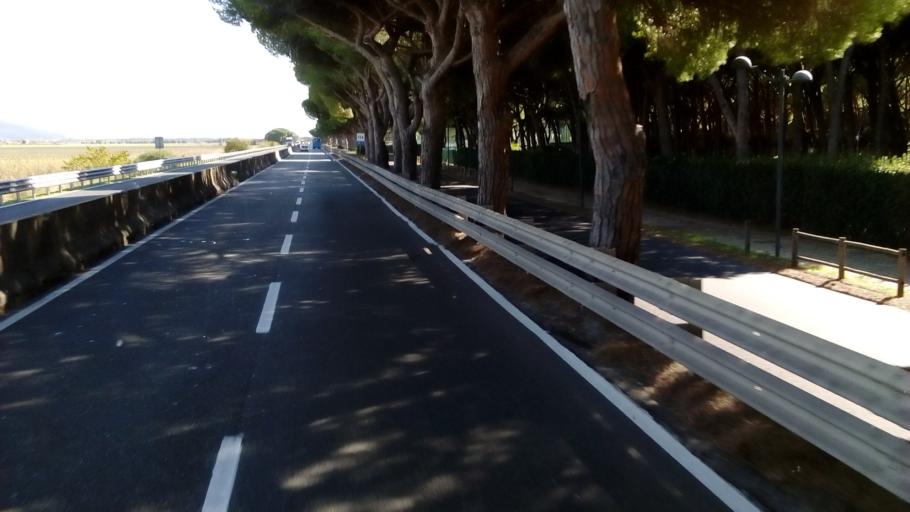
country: IT
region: Tuscany
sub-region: Provincia di Grosseto
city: Fonteblanda
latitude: 42.5316
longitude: 11.1866
